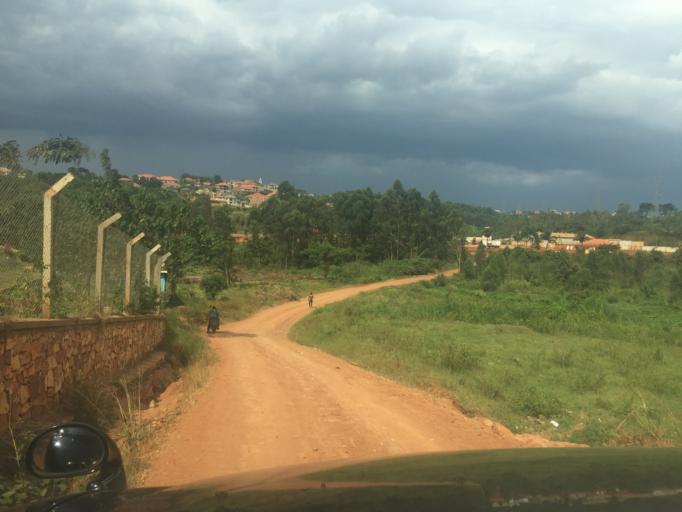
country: UG
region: Central Region
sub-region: Wakiso District
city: Kireka
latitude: 0.4072
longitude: 32.6276
